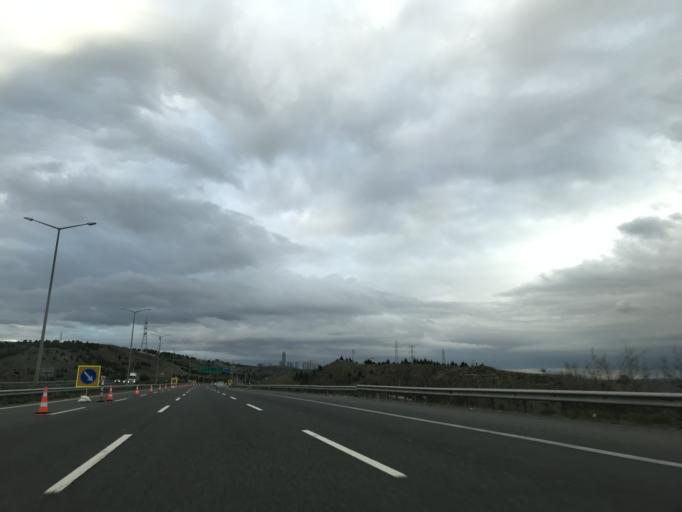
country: TR
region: Ankara
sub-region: Goelbasi
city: Golbasi
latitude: 39.8019
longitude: 32.7926
